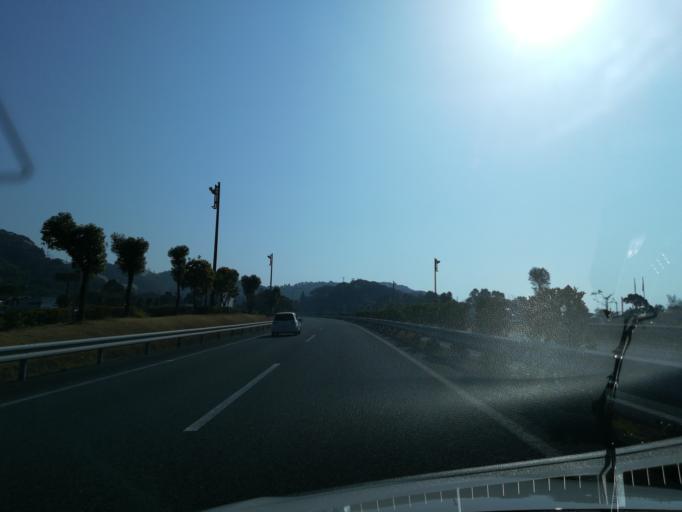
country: JP
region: Kochi
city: Kochi-shi
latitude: 33.6016
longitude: 133.6138
